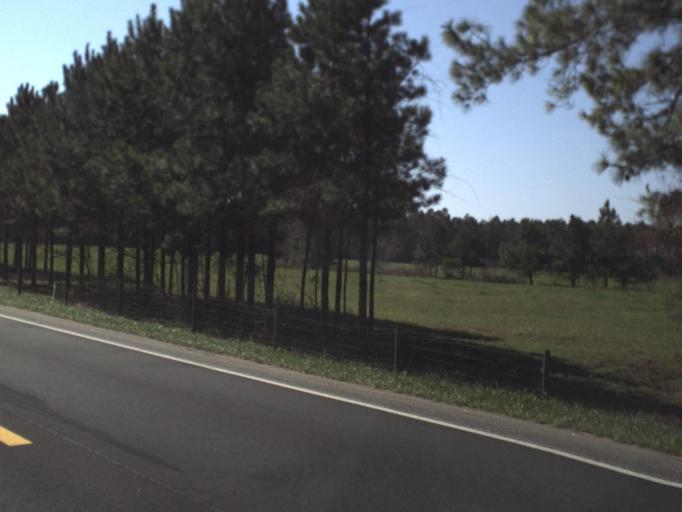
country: US
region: Florida
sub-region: Jackson County
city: Marianna
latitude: 30.6891
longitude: -85.1783
